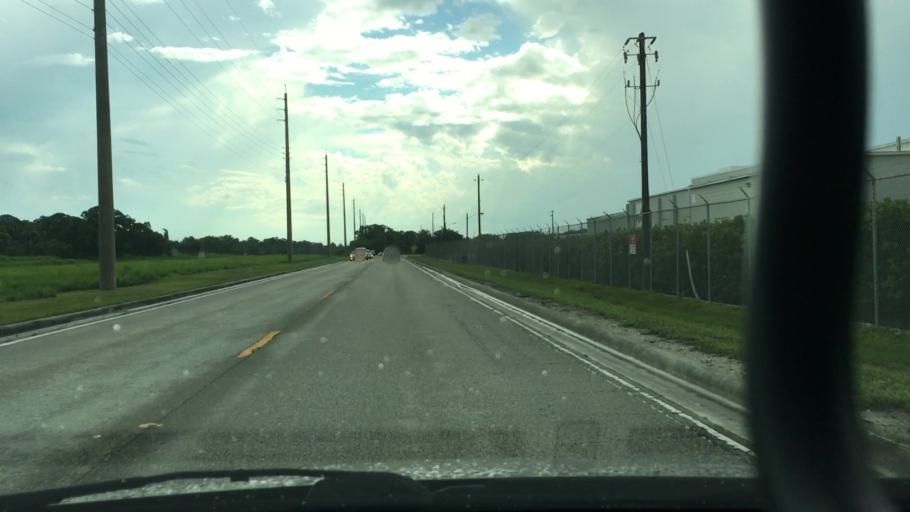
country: US
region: Florida
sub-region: Indian River County
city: Vero Beach
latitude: 27.6471
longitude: -80.4088
